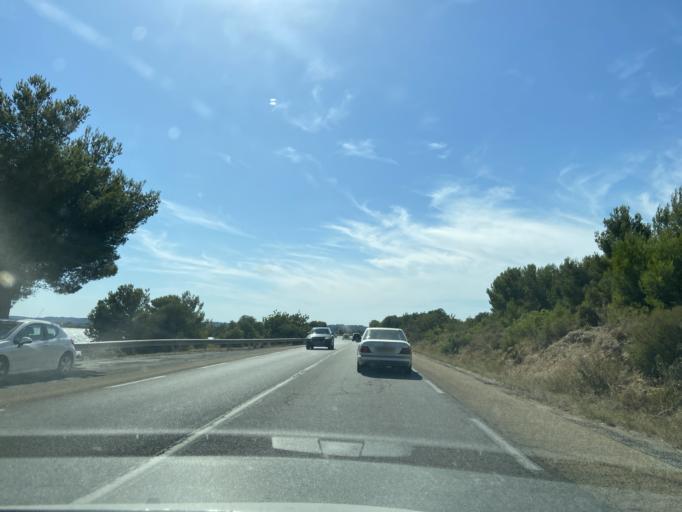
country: FR
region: Provence-Alpes-Cote d'Azur
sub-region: Departement des Bouches-du-Rhone
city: Saint-Chamas
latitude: 43.5283
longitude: 5.0623
